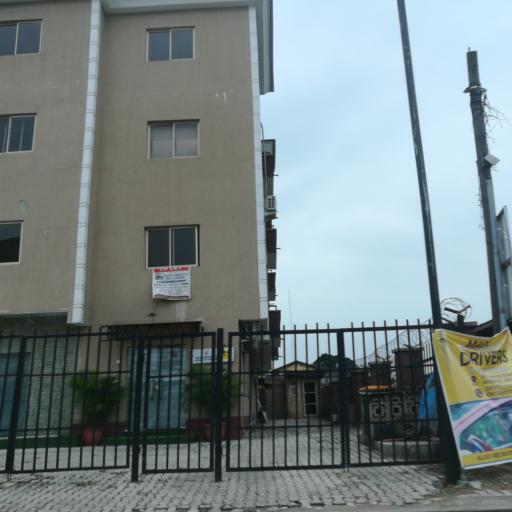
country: NG
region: Lagos
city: Makoko
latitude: 6.4990
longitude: 3.3800
